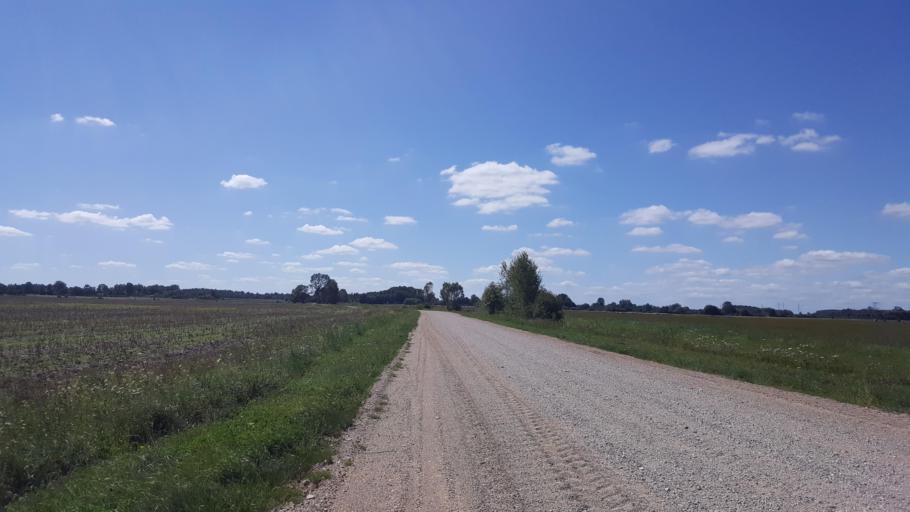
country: BY
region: Brest
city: Horad Kobryn
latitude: 52.3097
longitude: 24.3796
